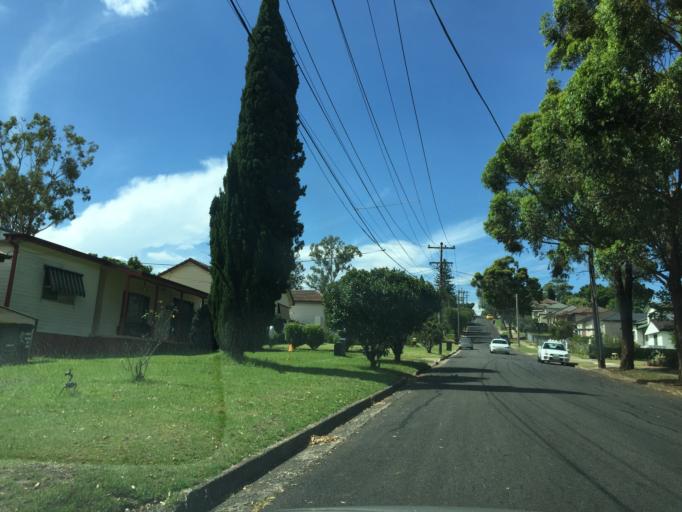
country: AU
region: New South Wales
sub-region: Blacktown
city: Doonside
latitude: -33.7814
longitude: 150.8900
